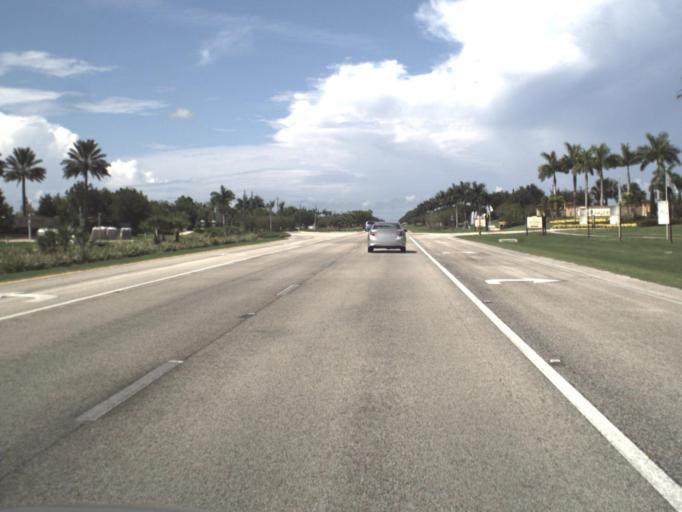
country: US
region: Florida
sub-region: Sarasota County
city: Plantation
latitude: 27.0497
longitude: -82.3420
